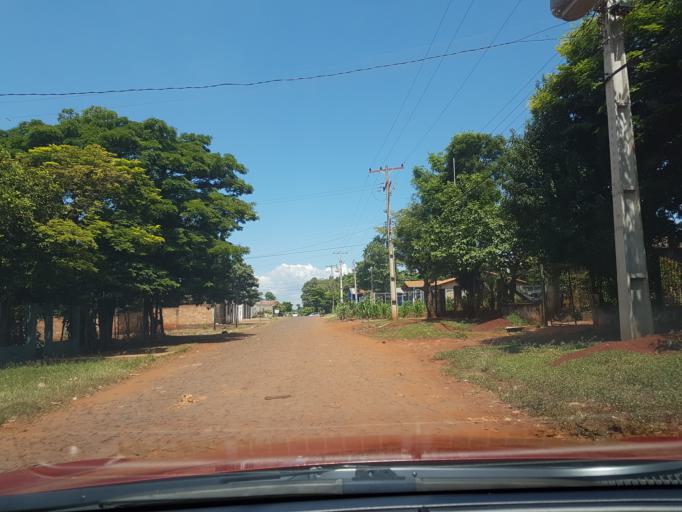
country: PY
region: Alto Parana
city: Ciudad del Este
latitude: -25.4806
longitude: -54.6800
